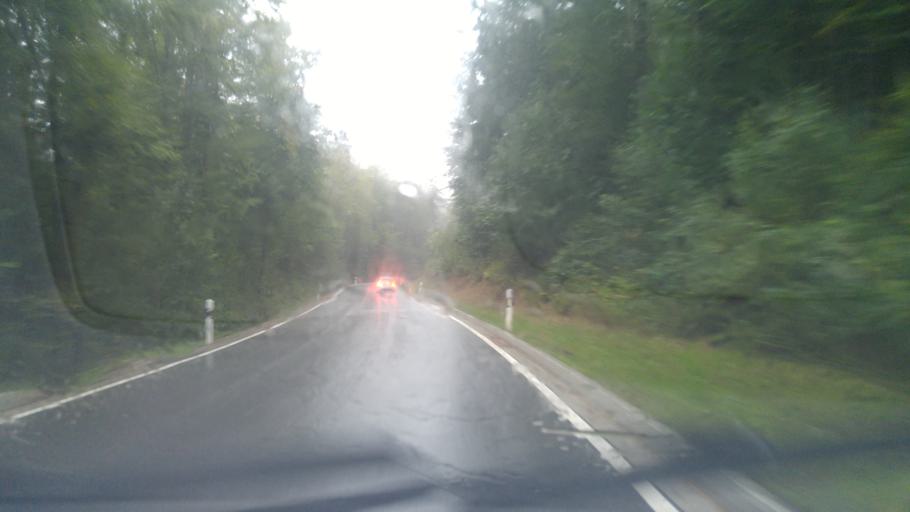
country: DE
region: Rheinland-Pfalz
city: Birkenhordt
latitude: 49.1175
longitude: 7.9191
